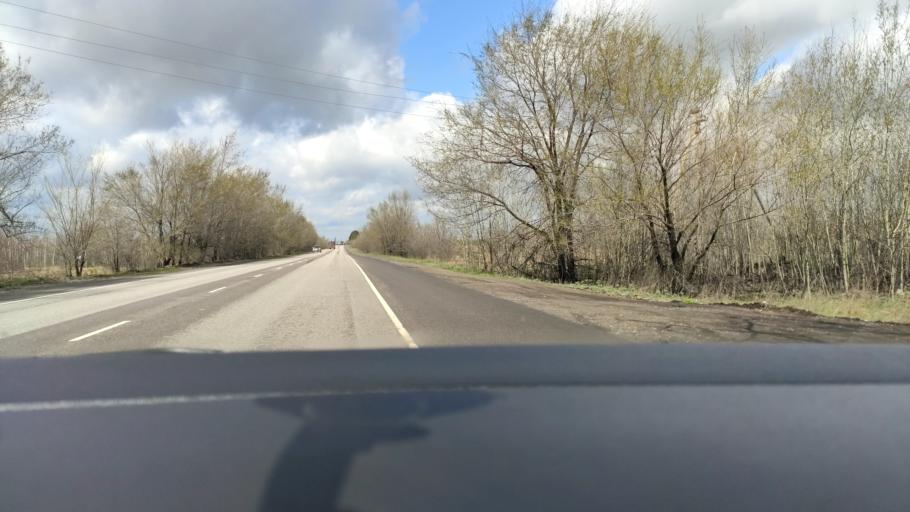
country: RU
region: Voronezj
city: Maslovka
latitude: 51.5610
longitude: 39.2757
